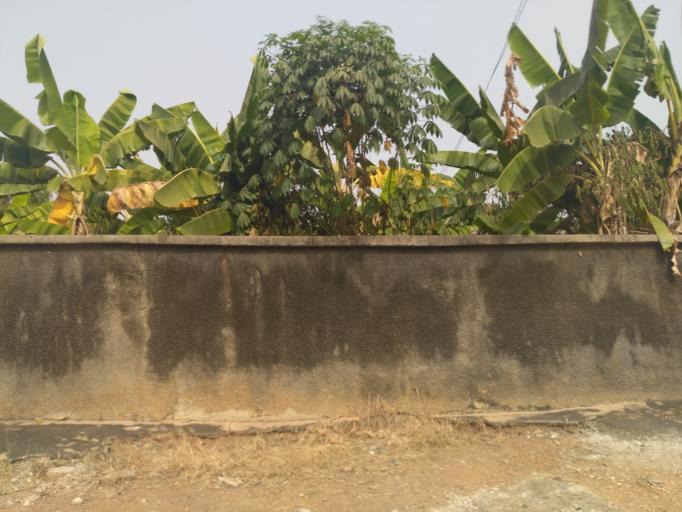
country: GH
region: Ashanti
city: Kumasi
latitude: 6.6753
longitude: -1.6057
